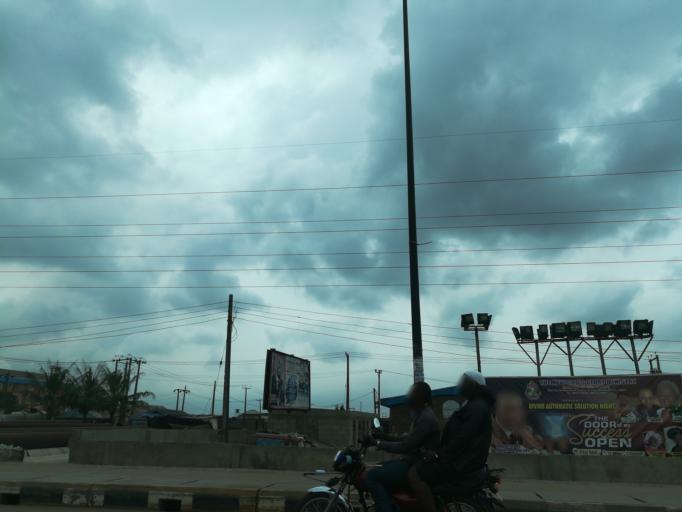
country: NG
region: Lagos
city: Ojota
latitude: 6.6068
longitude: 3.4079
